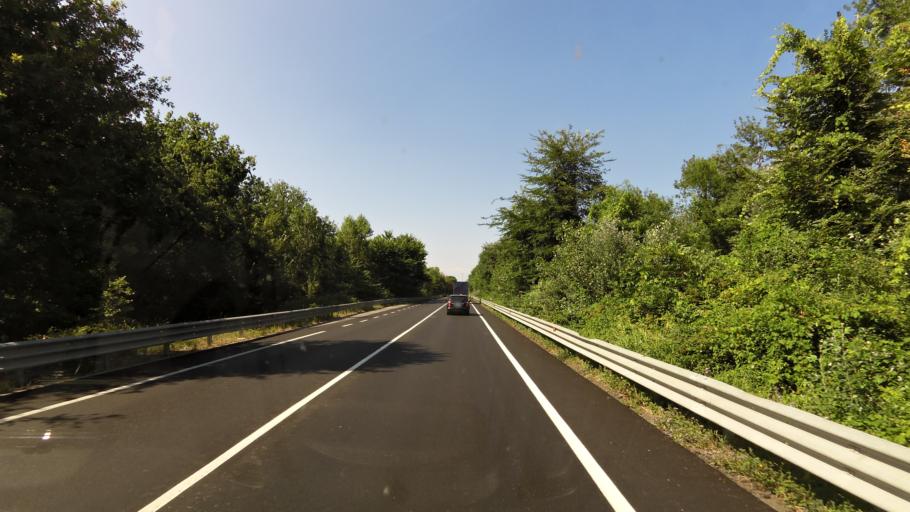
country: IT
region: Emilia-Romagna
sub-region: Provincia di Ravenna
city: Marina Romea
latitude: 44.5203
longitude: 12.2277
